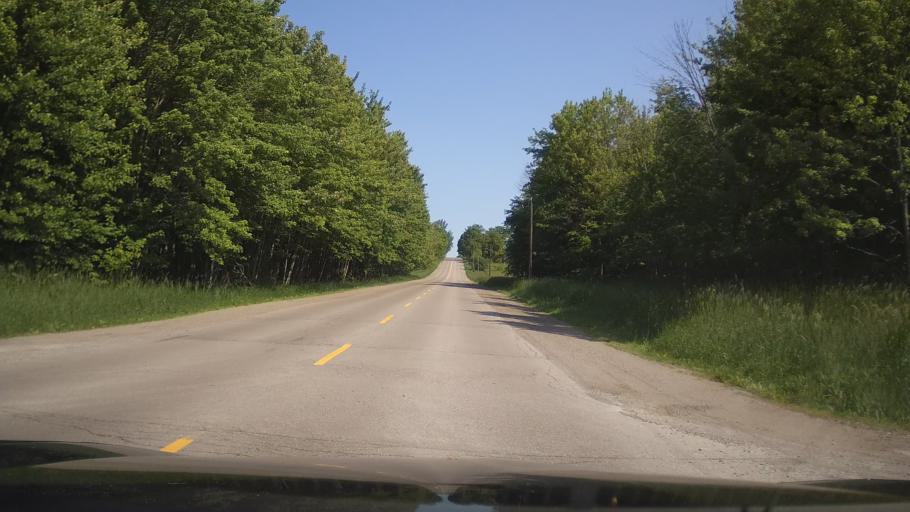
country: CA
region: Ontario
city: Uxbridge
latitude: 44.5240
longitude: -78.9620
